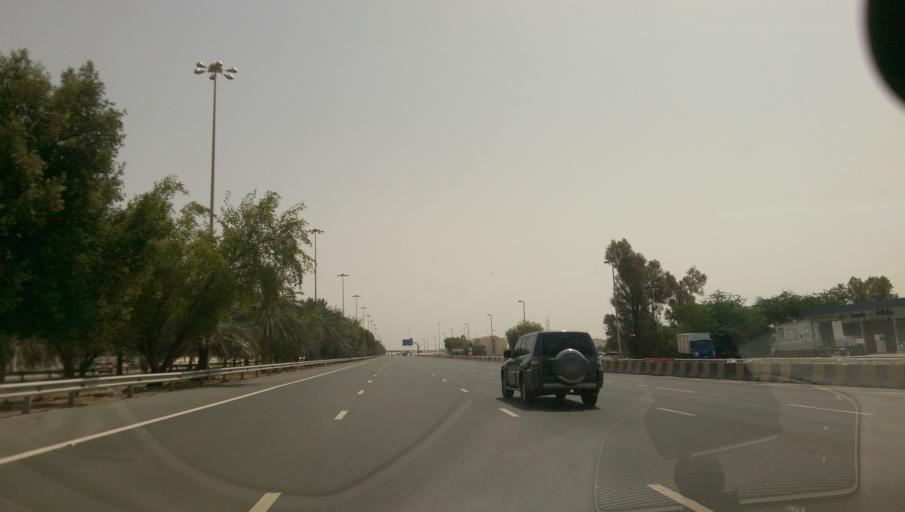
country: AE
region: Abu Dhabi
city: Abu Dhabi
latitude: 24.3218
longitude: 54.6152
